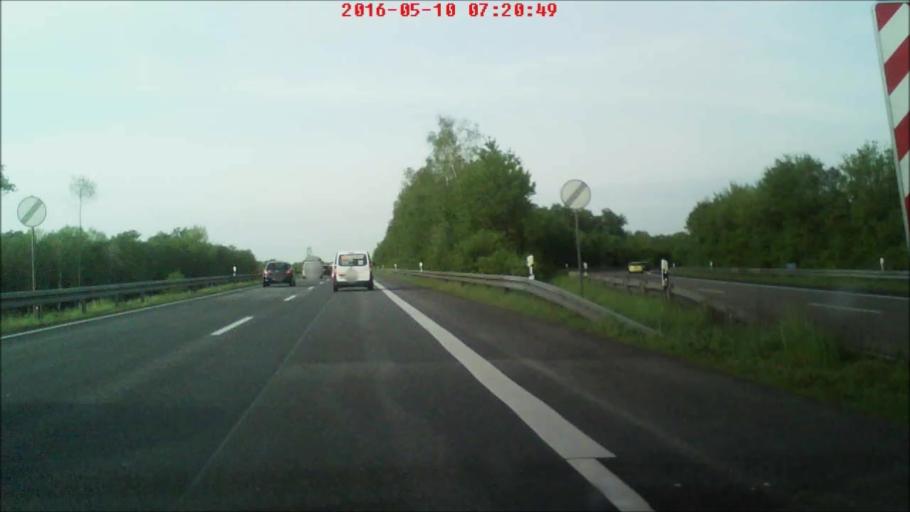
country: DE
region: Hesse
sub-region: Regierungsbezirk Darmstadt
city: Erlensee
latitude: 50.1399
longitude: 8.9874
